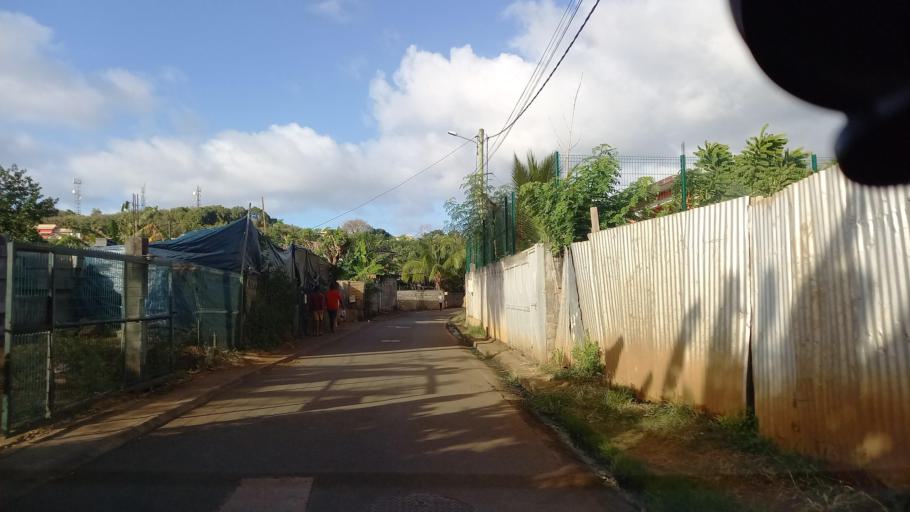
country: YT
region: Bandrele
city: Bandrele
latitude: -12.9126
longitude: 45.1948
